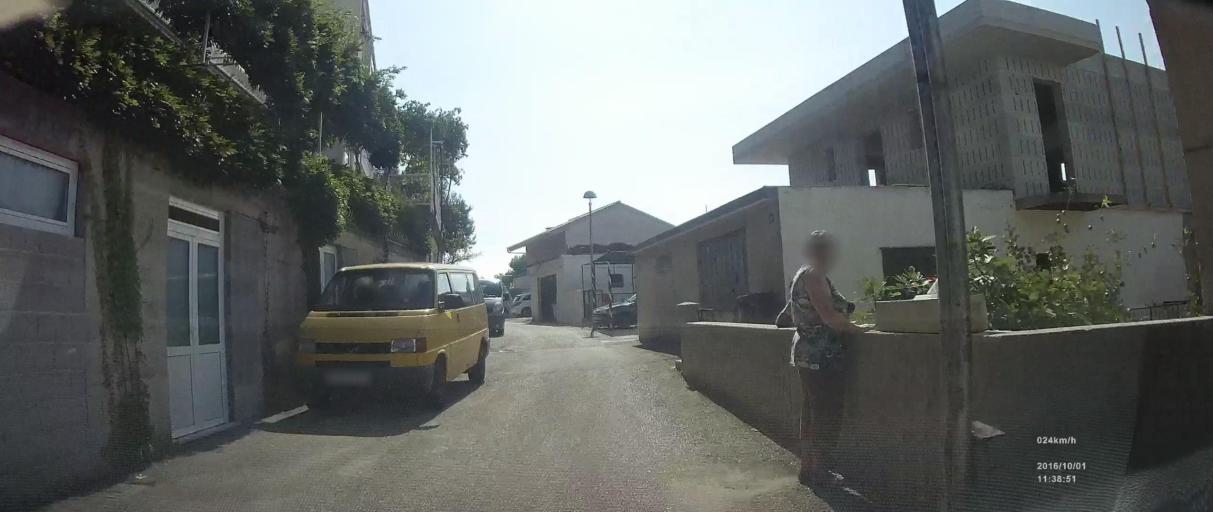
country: HR
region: Splitsko-Dalmatinska
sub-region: Grad Omis
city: Omis
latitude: 43.4393
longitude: 16.6993
